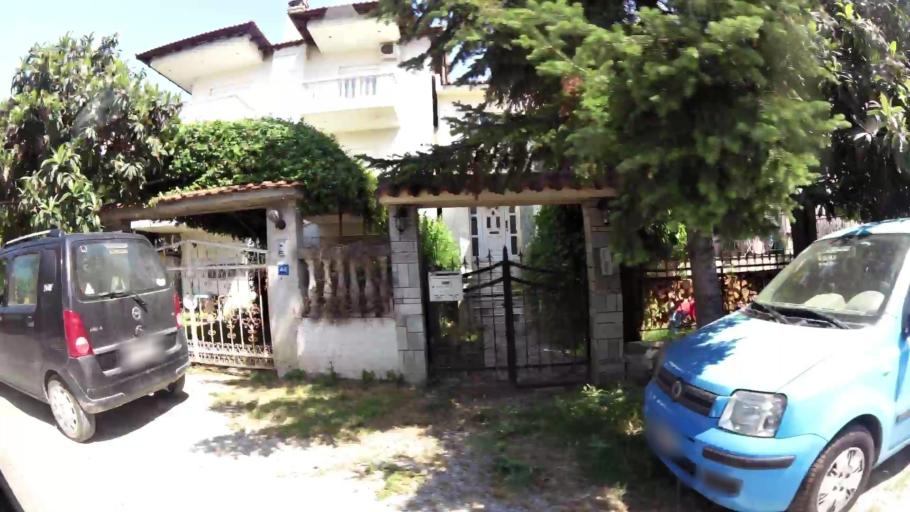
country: GR
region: Central Macedonia
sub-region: Nomos Thessalonikis
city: Neoi Epivates
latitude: 40.5006
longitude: 22.9027
